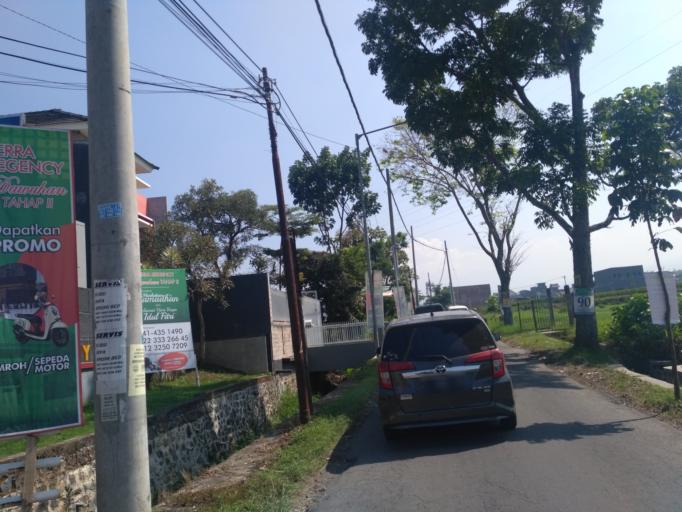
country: ID
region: East Java
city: Batu
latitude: -7.9092
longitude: 112.5868
